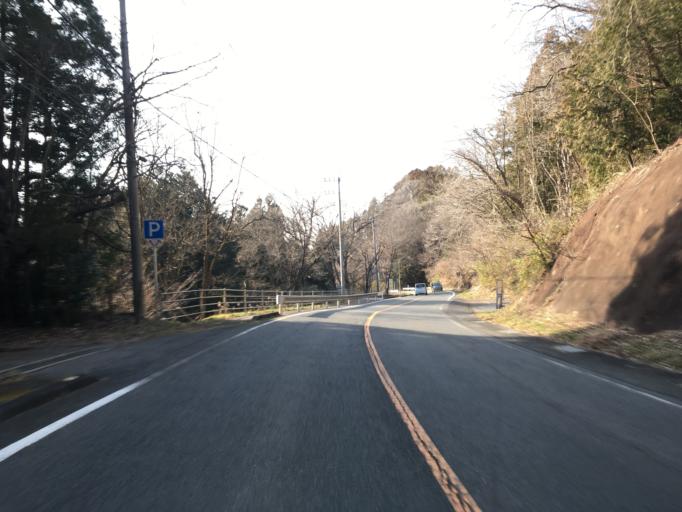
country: JP
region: Ibaraki
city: Daigo
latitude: 36.7496
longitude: 140.3970
